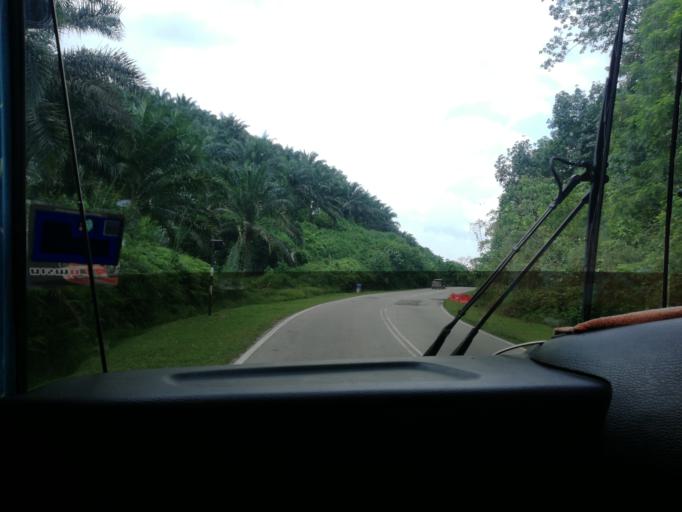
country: MY
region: Kedah
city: Kulim
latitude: 5.3435
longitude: 100.5868
